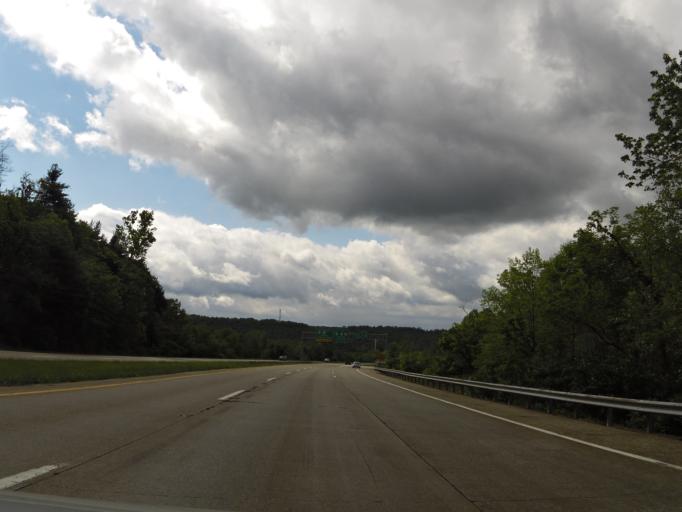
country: US
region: Ohio
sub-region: Athens County
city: Athens
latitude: 39.3438
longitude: -82.0813
